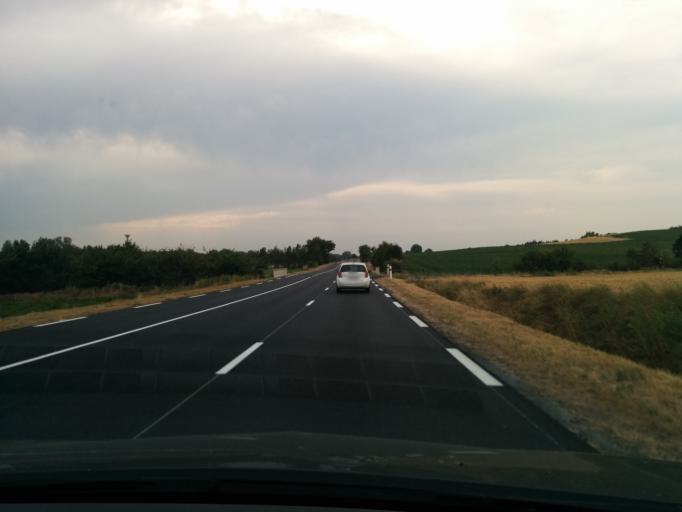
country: FR
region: Languedoc-Roussillon
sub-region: Departement de l'Aude
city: Villepinte
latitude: 43.2726
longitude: 2.1087
